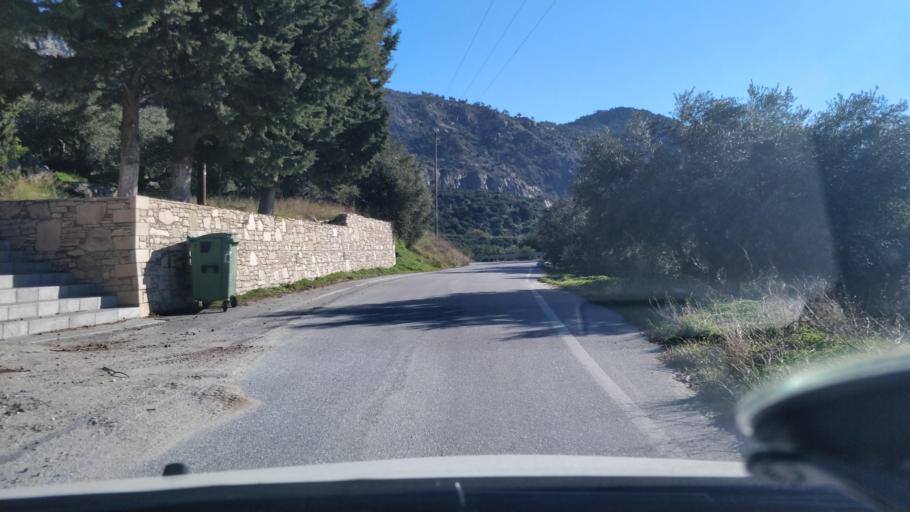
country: GR
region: Crete
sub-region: Nomos Lasithiou
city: Kritsa
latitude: 35.0794
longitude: 25.5916
